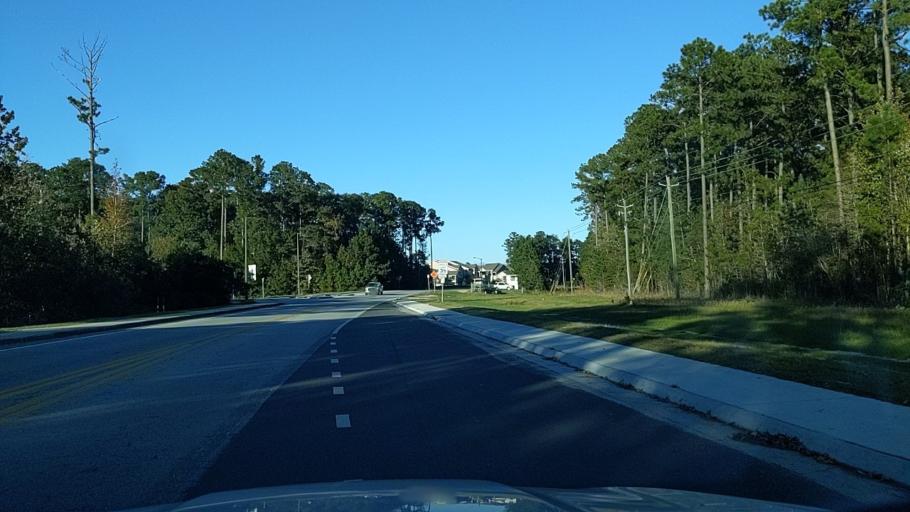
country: US
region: Georgia
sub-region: Chatham County
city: Pooler
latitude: 32.1733
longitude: -81.2333
